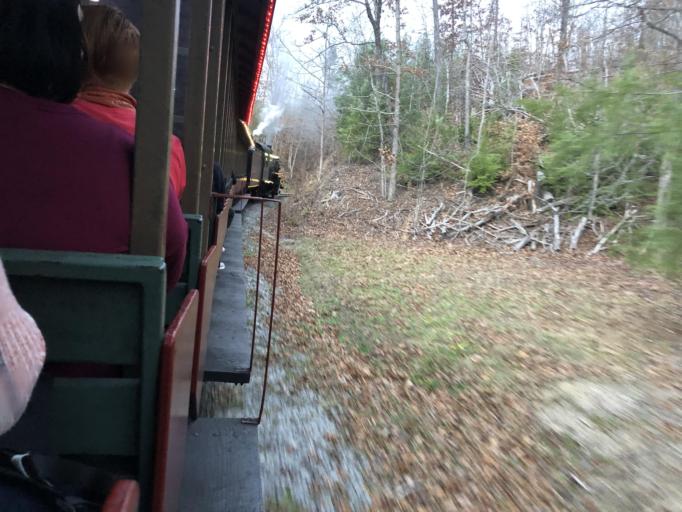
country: US
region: Tennessee
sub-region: Sevier County
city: Pigeon Forge
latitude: 35.7974
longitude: -83.5291
